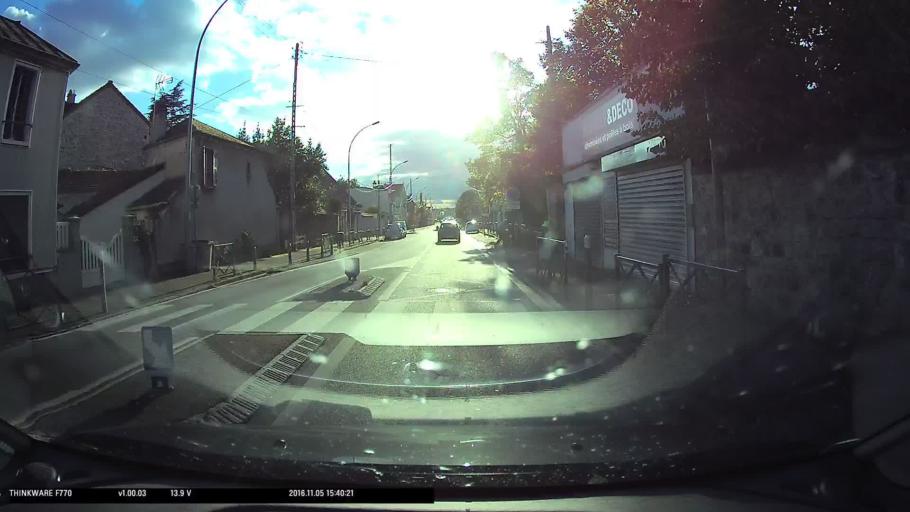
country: FR
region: Ile-de-France
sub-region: Departement des Yvelines
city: Les Mureaux
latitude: 48.9951
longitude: 1.9067
